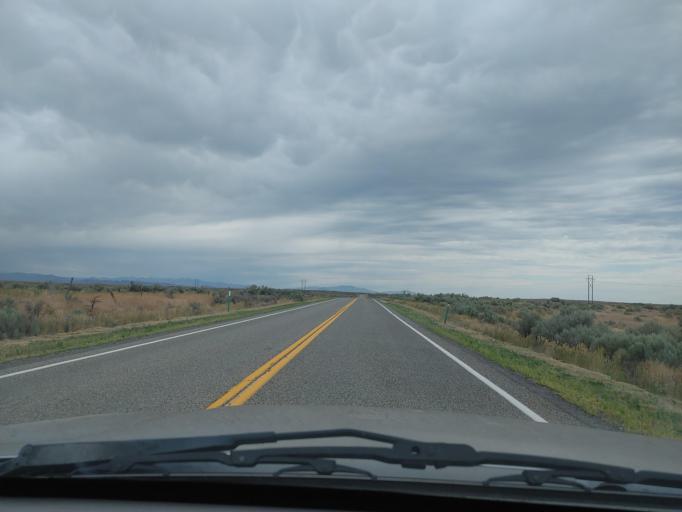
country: US
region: Idaho
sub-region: Lincoln County
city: Shoshone
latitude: 43.0843
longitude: -114.0985
